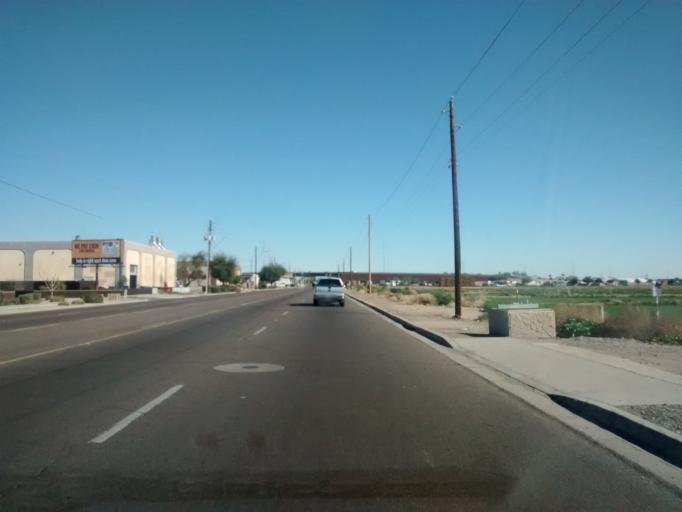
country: US
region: Arizona
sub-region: Maricopa County
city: Glendale
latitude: 33.5240
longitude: -112.1755
